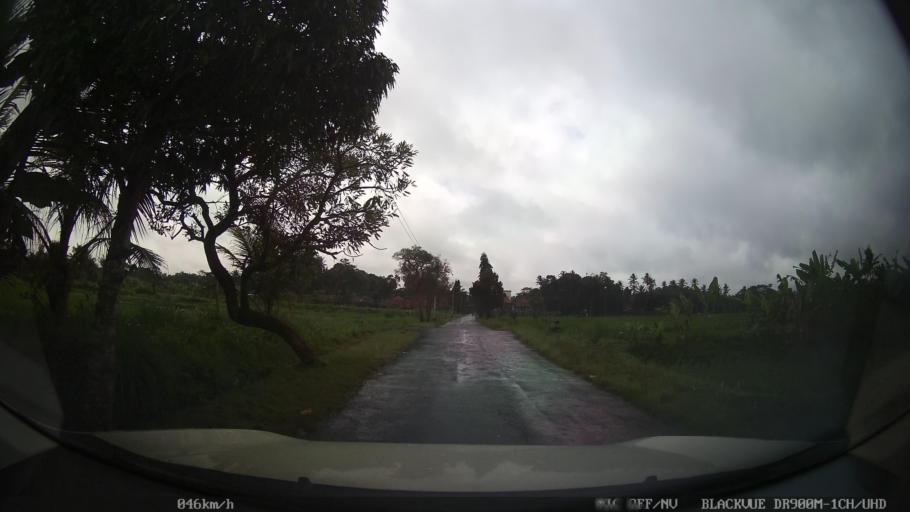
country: ID
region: Bali
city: Pegongan
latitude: -8.4952
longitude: 115.2259
